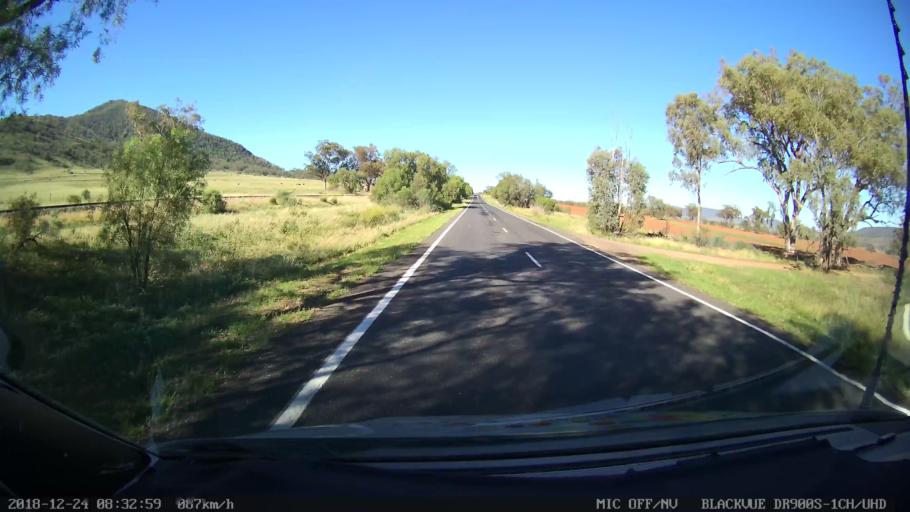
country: AU
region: New South Wales
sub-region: Tamworth Municipality
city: Phillip
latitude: -31.2835
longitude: 150.6905
